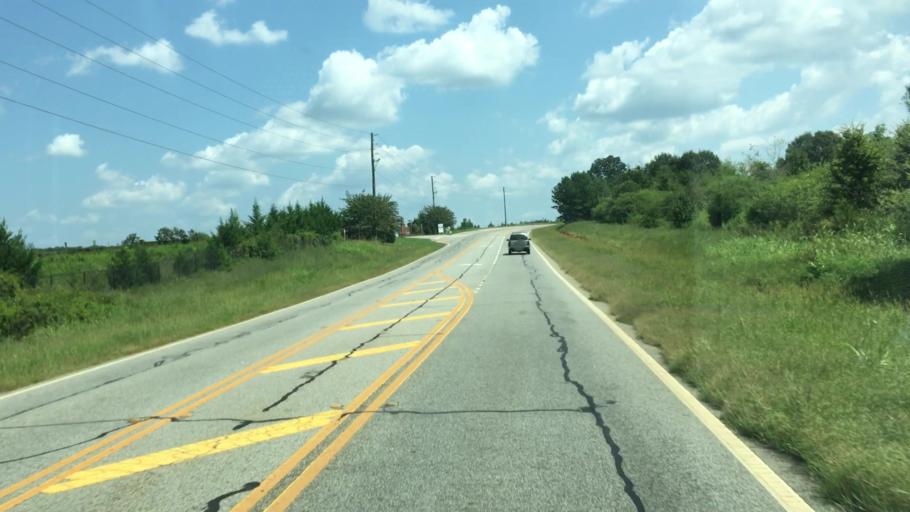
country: US
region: Georgia
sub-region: Barrow County
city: Statham
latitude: 33.9361
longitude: -83.6267
